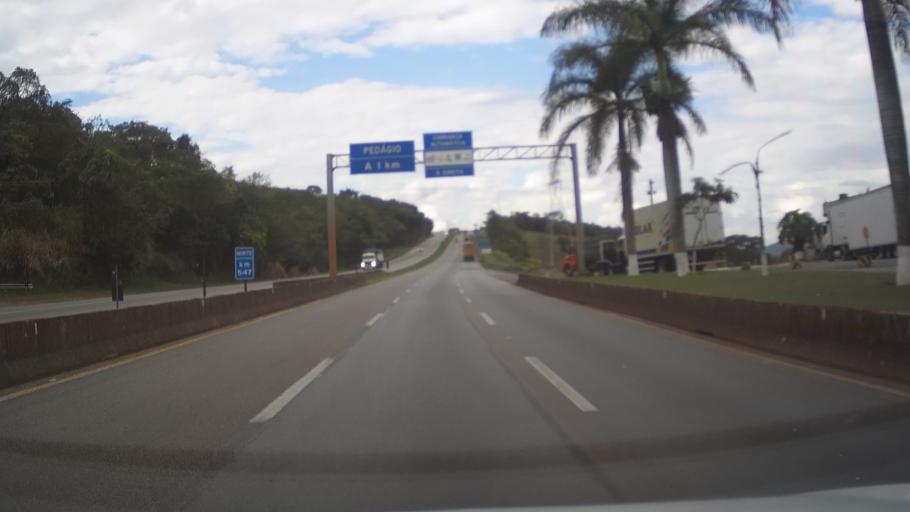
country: BR
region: Minas Gerais
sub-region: Igarape
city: Igarape
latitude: -20.2772
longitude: -44.4272
